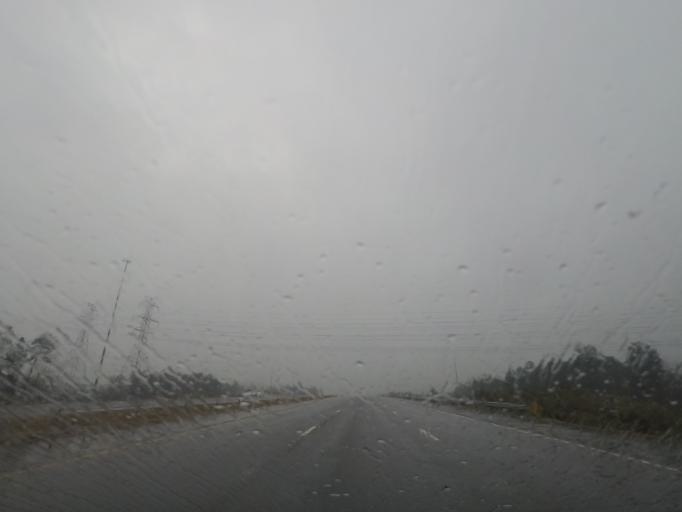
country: US
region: North Carolina
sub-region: Wake County
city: Morrisville
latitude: 35.8750
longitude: -78.8665
